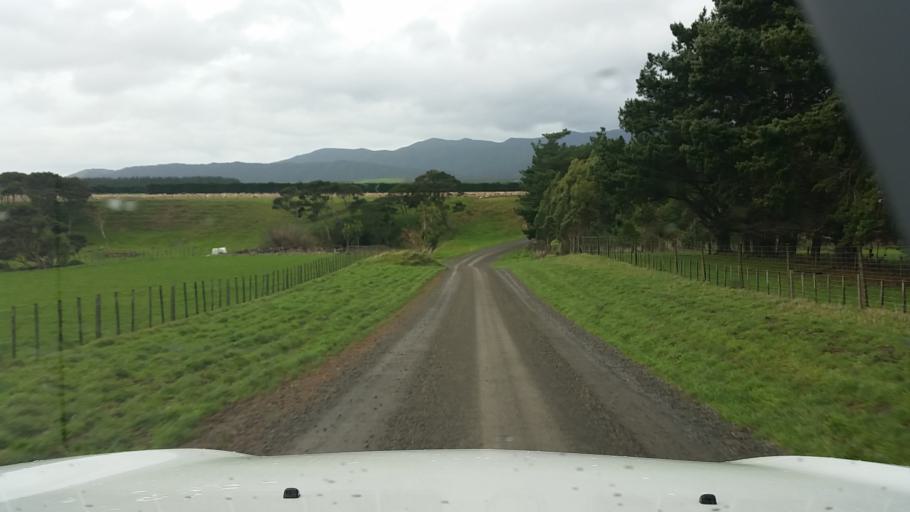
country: NZ
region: Wellington
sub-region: Upper Hutt City
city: Upper Hutt
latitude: -41.3429
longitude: 175.2257
